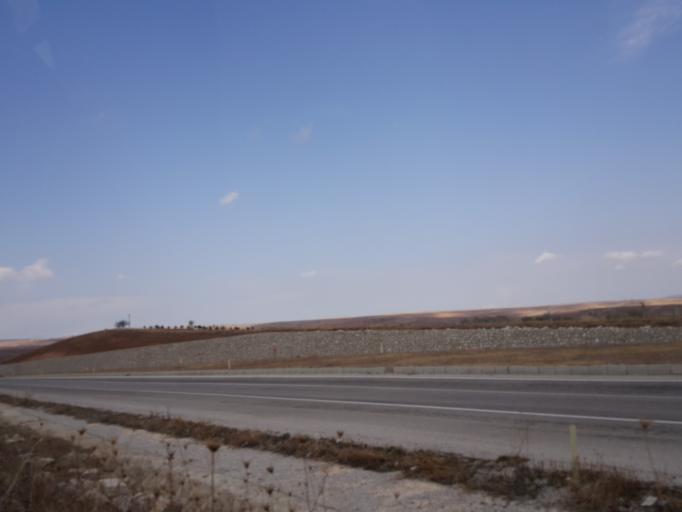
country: TR
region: Corum
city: Alaca
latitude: 40.1471
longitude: 34.7689
